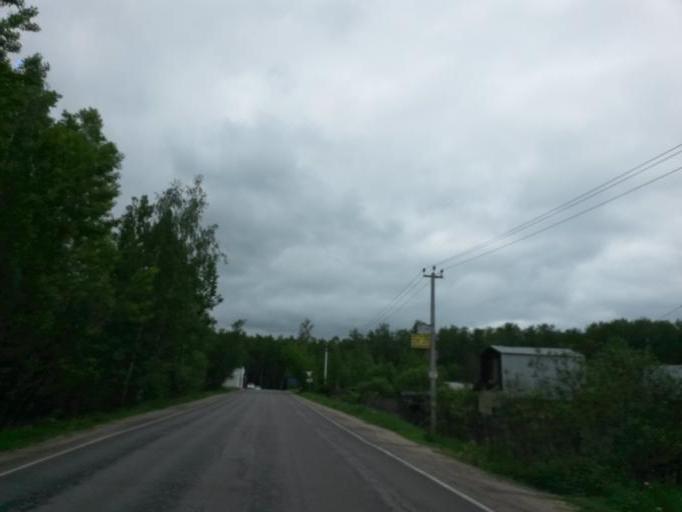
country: RU
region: Moskovskaya
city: Klimovsk
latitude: 55.3294
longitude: 37.6125
